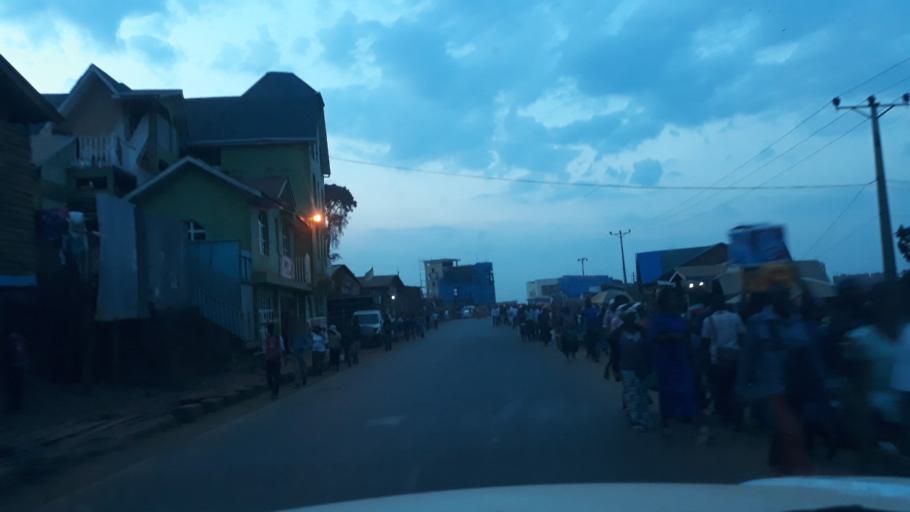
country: CD
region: South Kivu
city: Bukavu
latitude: -2.5253
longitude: 28.8539
